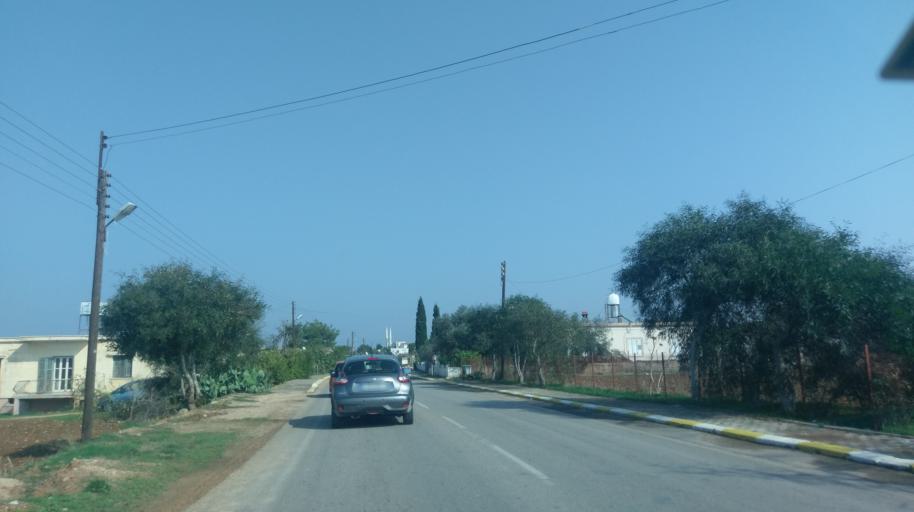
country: CY
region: Ammochostos
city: Leonarisso
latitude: 35.5279
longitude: 34.1819
